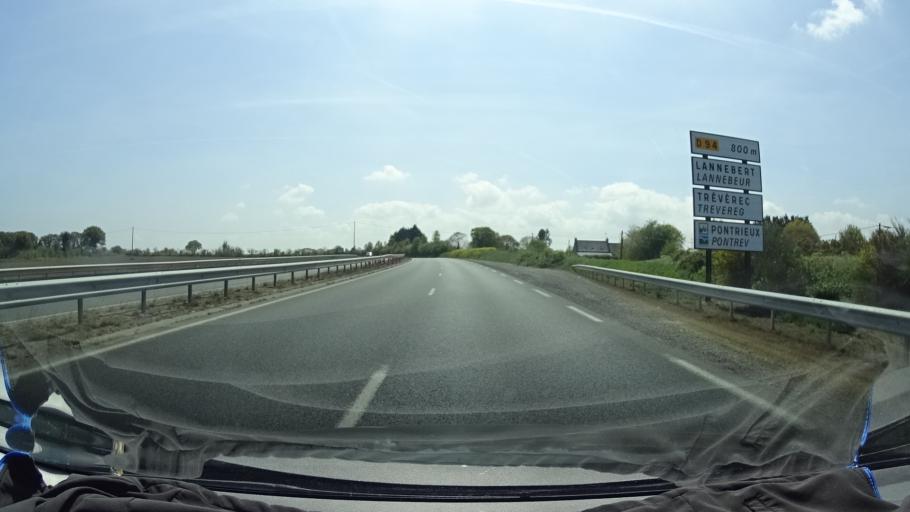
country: FR
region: Brittany
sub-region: Departement des Cotes-d'Armor
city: Plehedel
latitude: 48.6665
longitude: -3.0247
